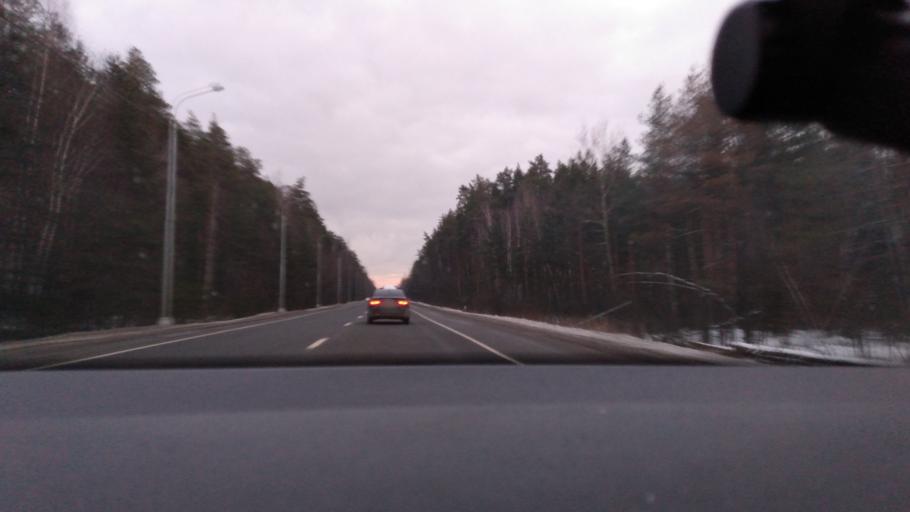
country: RU
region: Moskovskaya
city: Il'inskiy Pogost
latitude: 55.4676
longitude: 38.9685
